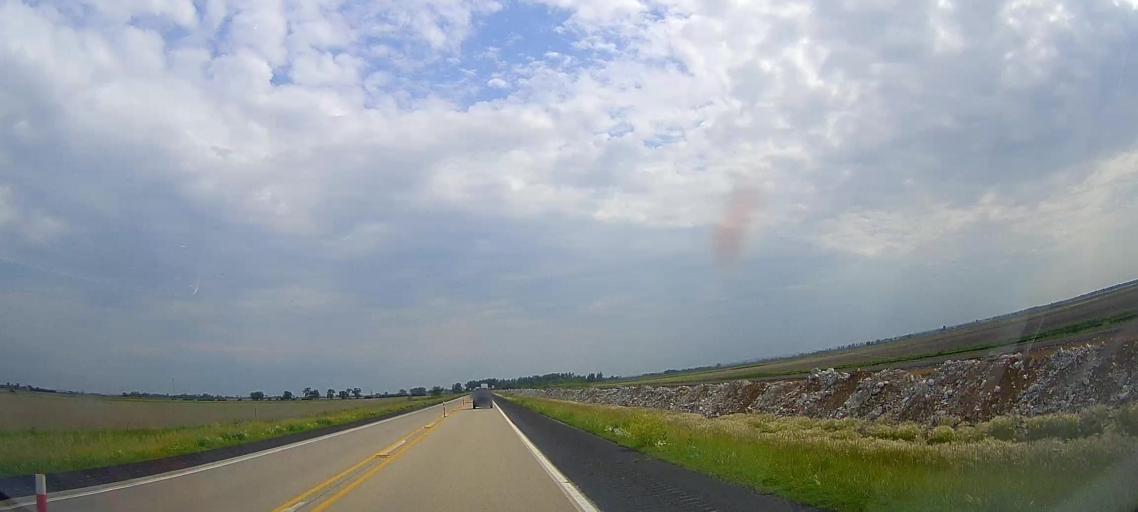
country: US
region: Nebraska
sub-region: Washington County
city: Blair
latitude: 41.6921
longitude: -96.0420
